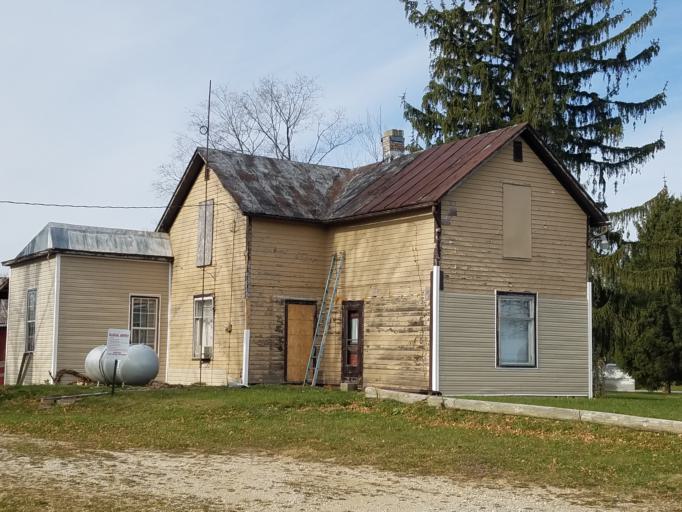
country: US
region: Ohio
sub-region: Morrow County
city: Mount Gilead
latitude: 40.5442
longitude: -82.7585
